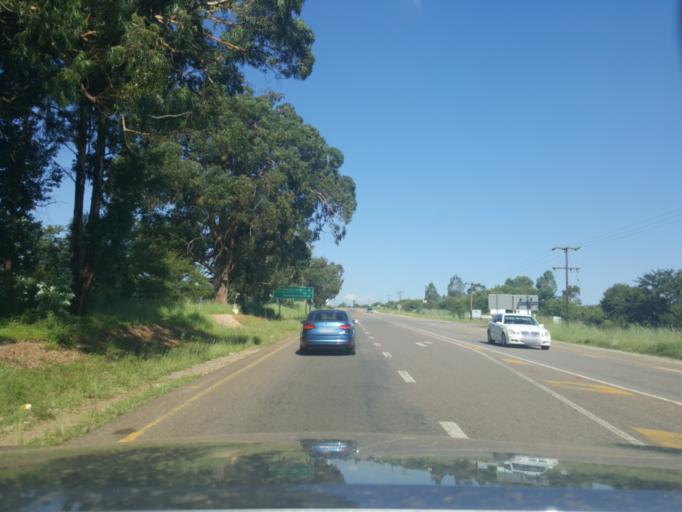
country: ZA
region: Gauteng
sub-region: City of Tshwane Metropolitan Municipality
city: Cullinan
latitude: -25.7727
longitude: 28.4510
